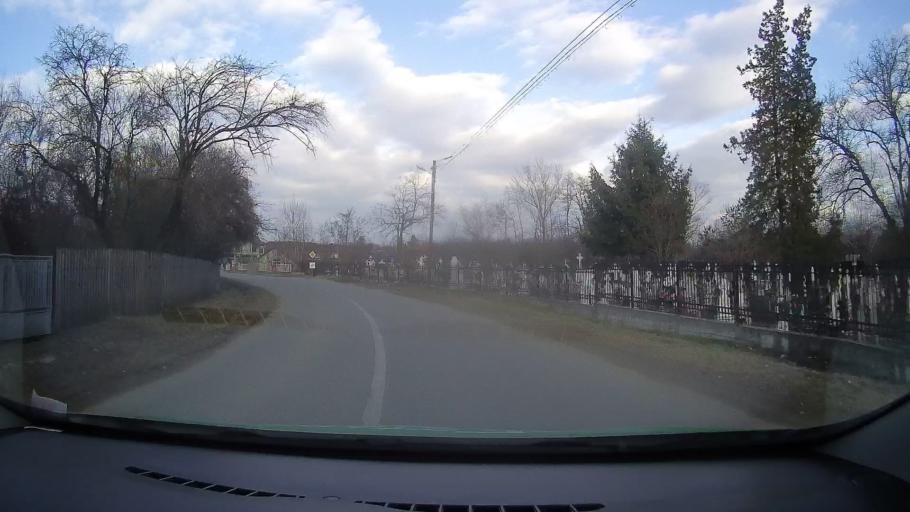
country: RO
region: Dambovita
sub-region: Comuna Gura Ocnitei
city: Gura Ocnitei
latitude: 44.9400
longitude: 25.5663
